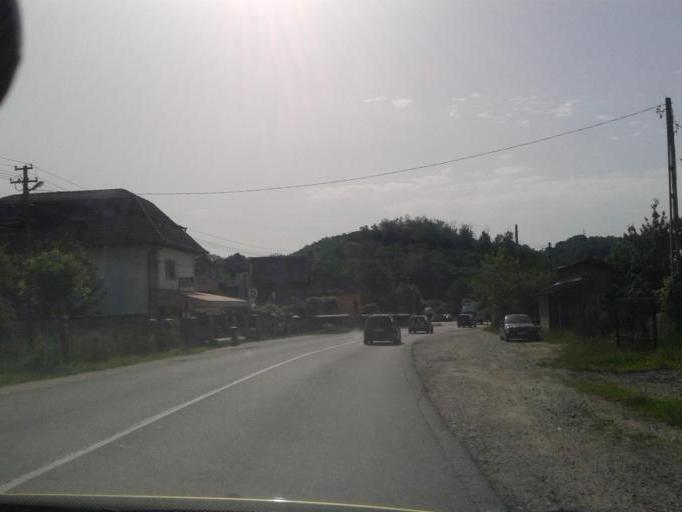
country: RO
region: Valcea
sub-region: Comuna Barbatesti
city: Bodesti
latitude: 45.1308
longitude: 24.1109
